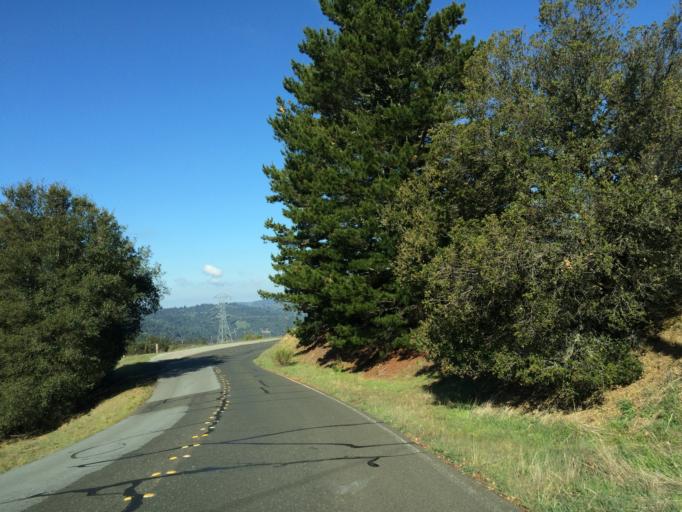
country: US
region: California
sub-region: Santa Clara County
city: Los Altos Hills
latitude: 37.3295
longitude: -122.1723
